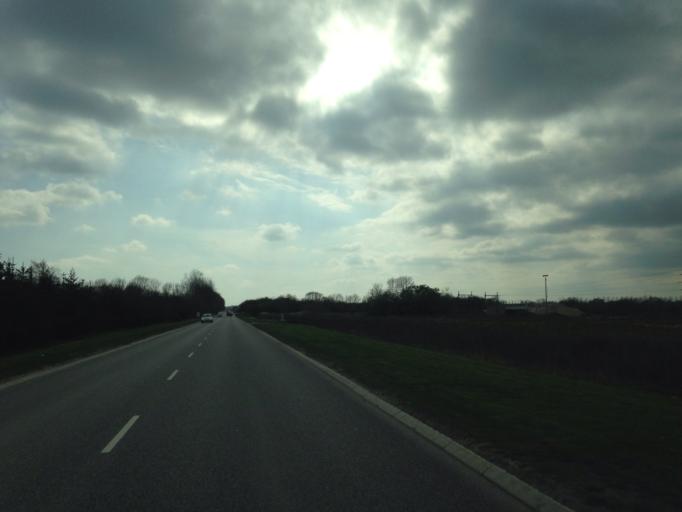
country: DK
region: Zealand
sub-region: Greve Kommune
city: Greve
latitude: 55.6138
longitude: 12.3101
